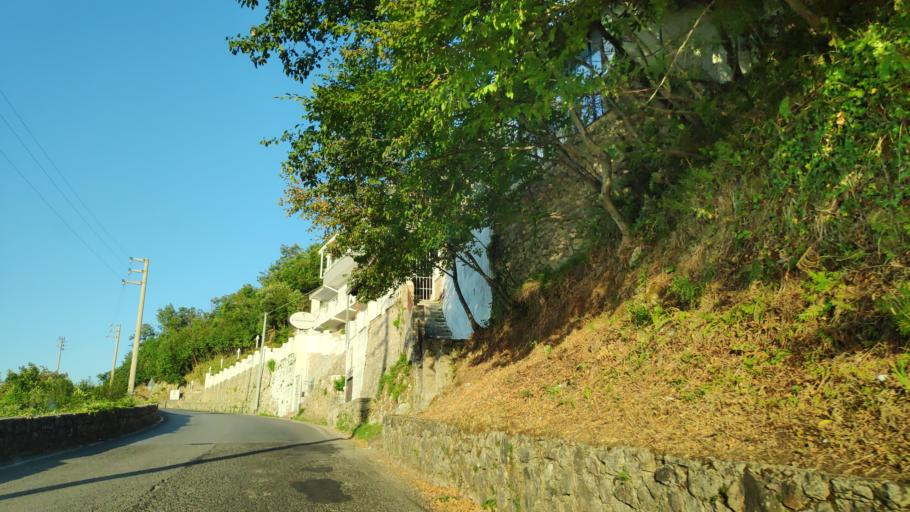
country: IT
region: Campania
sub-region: Provincia di Salerno
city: Corbara
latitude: 40.7247
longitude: 14.6028
